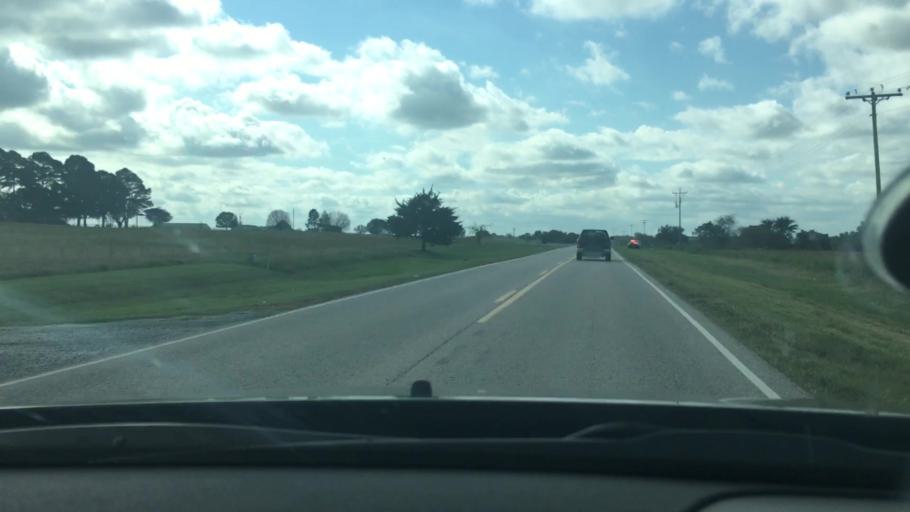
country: US
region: Oklahoma
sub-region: Pontotoc County
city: Ada
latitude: 34.7156
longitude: -96.6349
